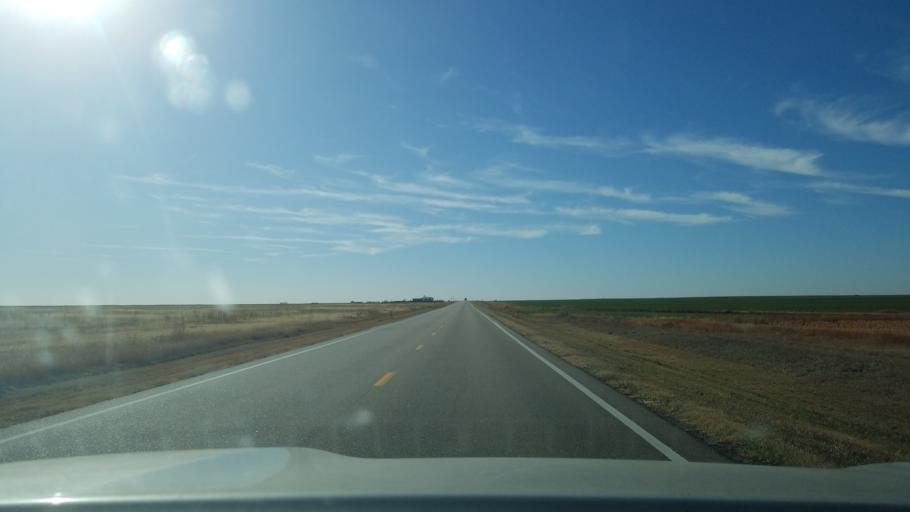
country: US
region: Kansas
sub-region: Ness County
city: Ness City
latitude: 38.3422
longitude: -99.8978
